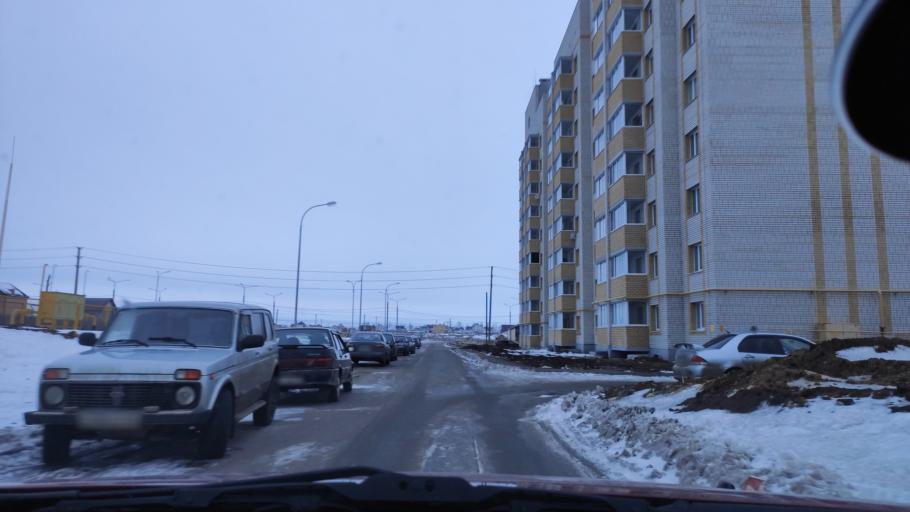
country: RU
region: Tambov
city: Tambov
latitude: 52.7833
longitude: 41.4190
